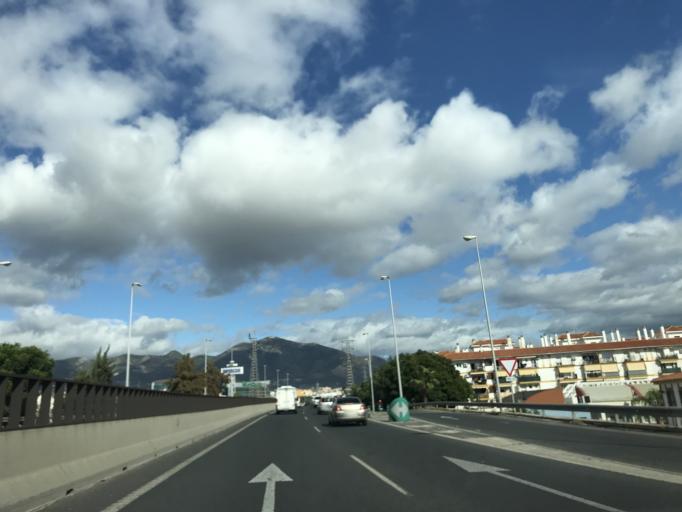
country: ES
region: Andalusia
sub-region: Provincia de Malaga
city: Fuengirola
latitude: 36.5441
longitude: -4.6340
